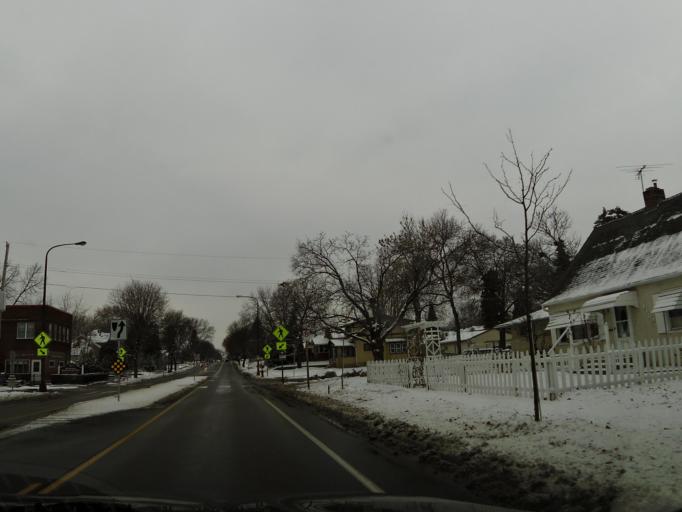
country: US
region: Minnesota
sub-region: Ramsey County
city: Saint Paul
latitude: 44.9776
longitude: -93.0501
